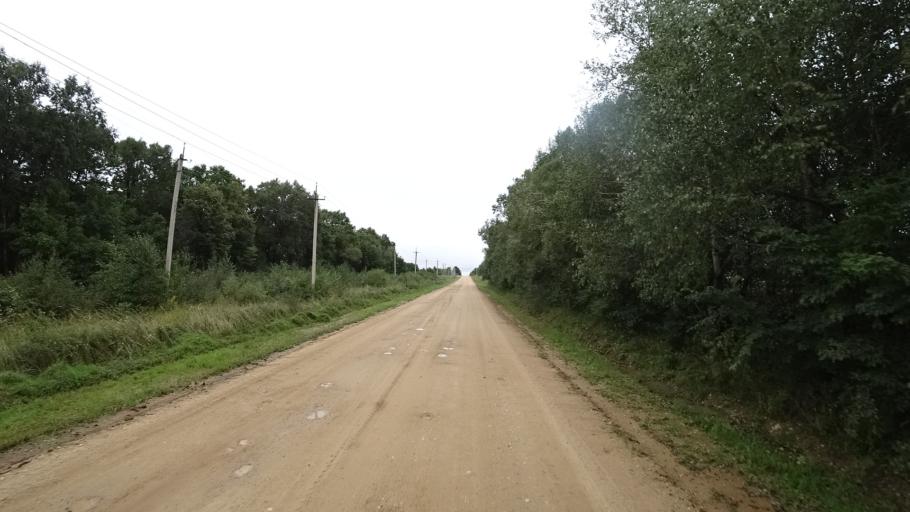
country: RU
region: Primorskiy
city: Monastyrishche
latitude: 44.0752
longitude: 132.5861
